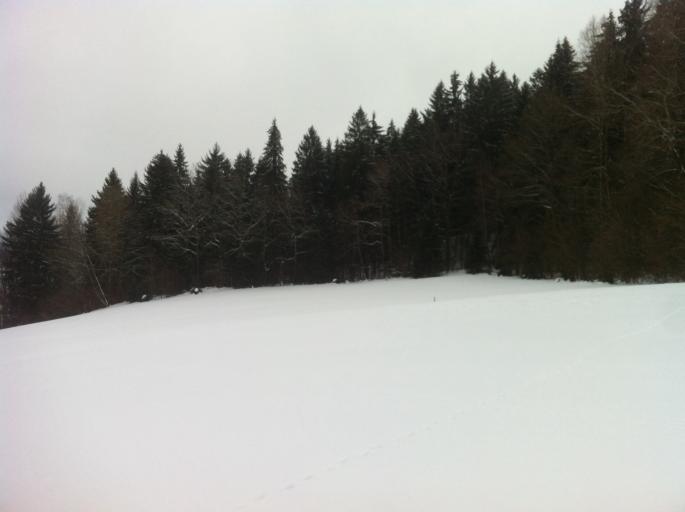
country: DE
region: Bavaria
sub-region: Lower Bavaria
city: Zwiesel
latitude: 49.0323
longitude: 13.2162
